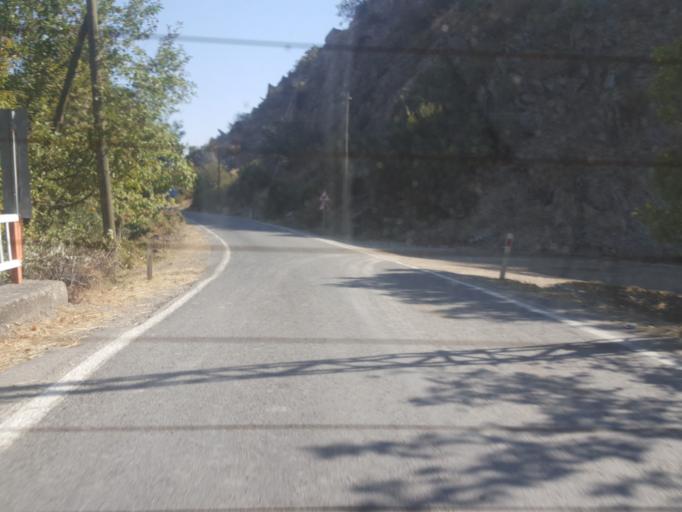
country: TR
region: Kastamonu
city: Tosya
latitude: 40.9847
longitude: 34.1000
